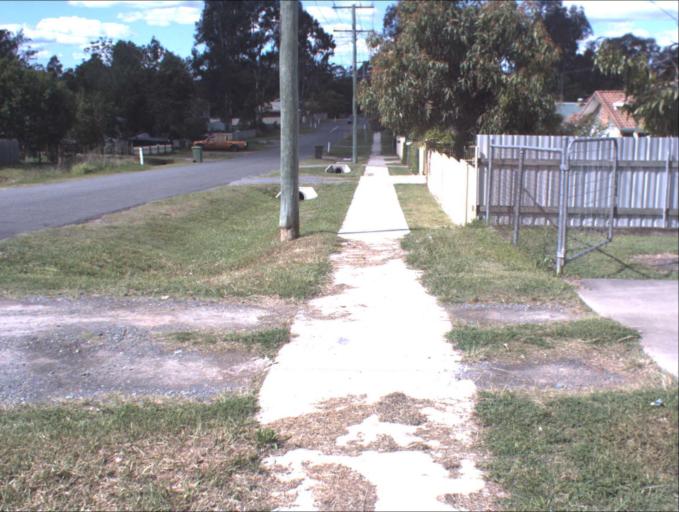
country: AU
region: Queensland
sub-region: Logan
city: Cedar Vale
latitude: -27.8297
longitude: 153.0299
